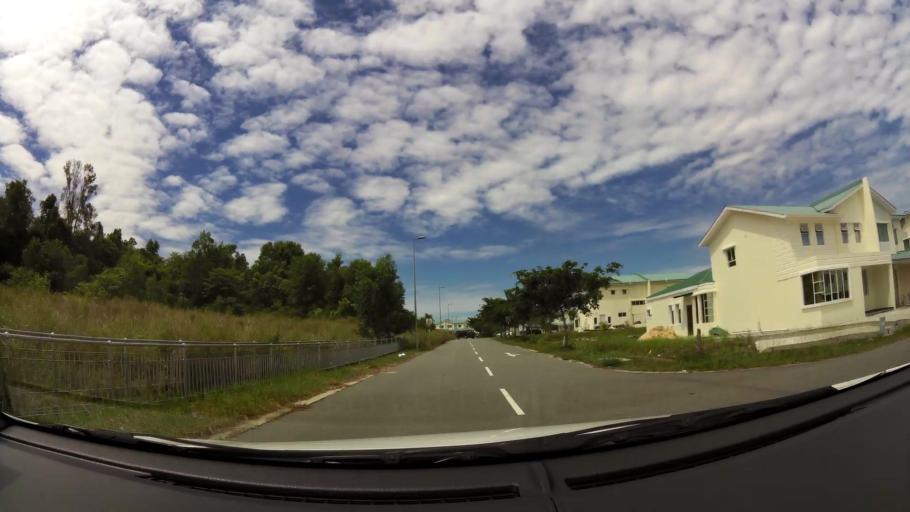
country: BN
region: Brunei and Muara
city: Bandar Seri Begawan
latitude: 4.9789
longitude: 115.0140
